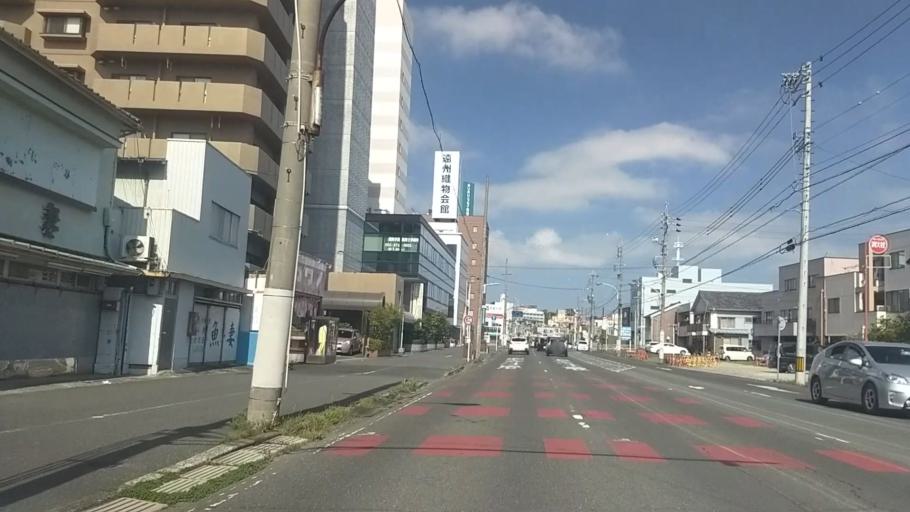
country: JP
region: Shizuoka
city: Hamamatsu
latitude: 34.7143
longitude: 137.7305
